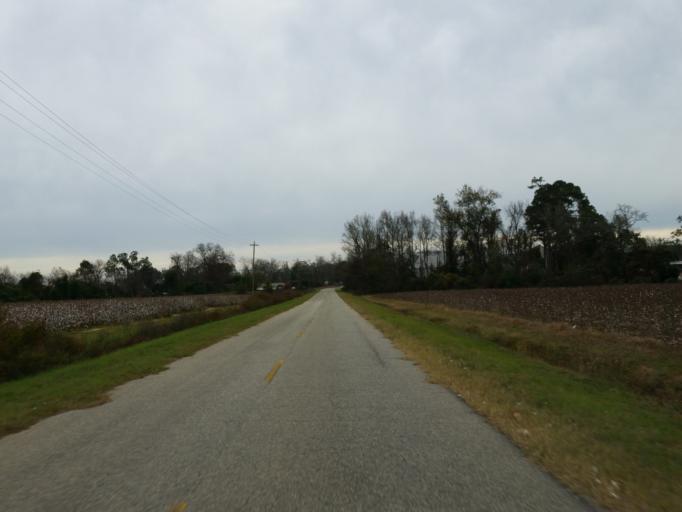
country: US
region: Georgia
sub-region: Dooly County
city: Vienna
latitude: 32.1576
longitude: -83.7733
